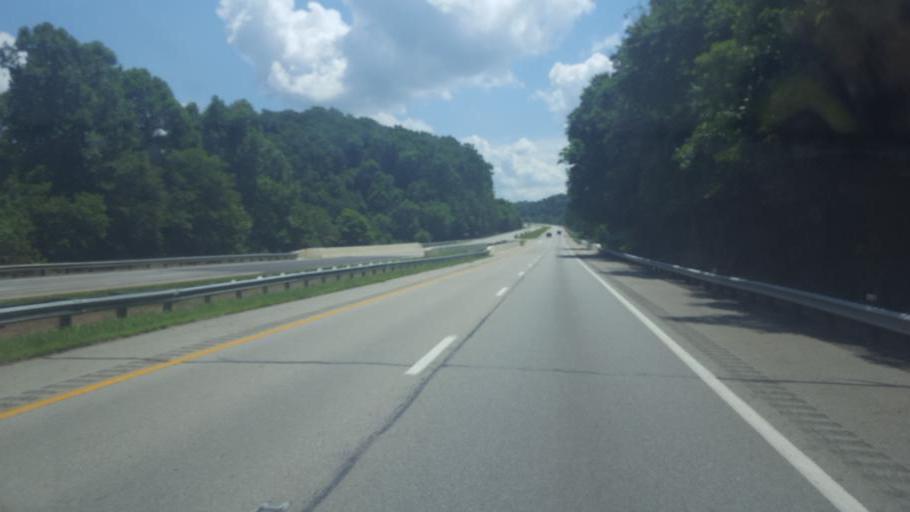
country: US
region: Ohio
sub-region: Jackson County
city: Jackson
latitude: 39.1051
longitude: -82.6733
